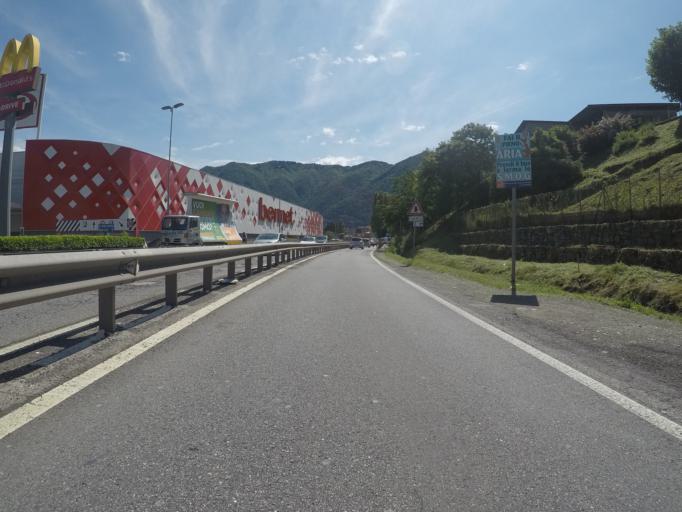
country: IT
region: Lombardy
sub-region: Provincia di Como
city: Cernobbio
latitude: 45.8370
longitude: 9.0624
